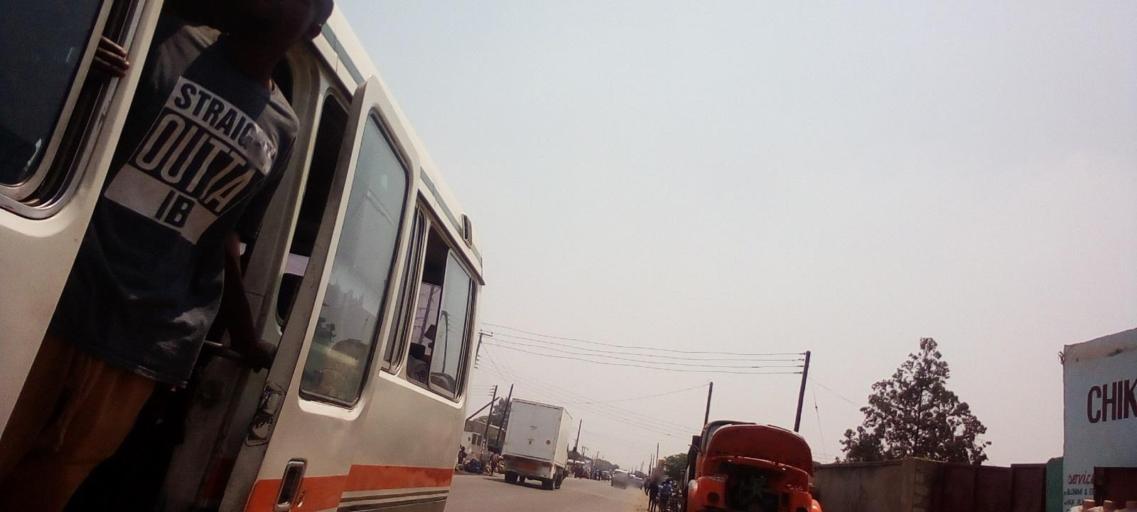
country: ZM
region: Lusaka
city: Lusaka
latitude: -15.4467
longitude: 28.2448
